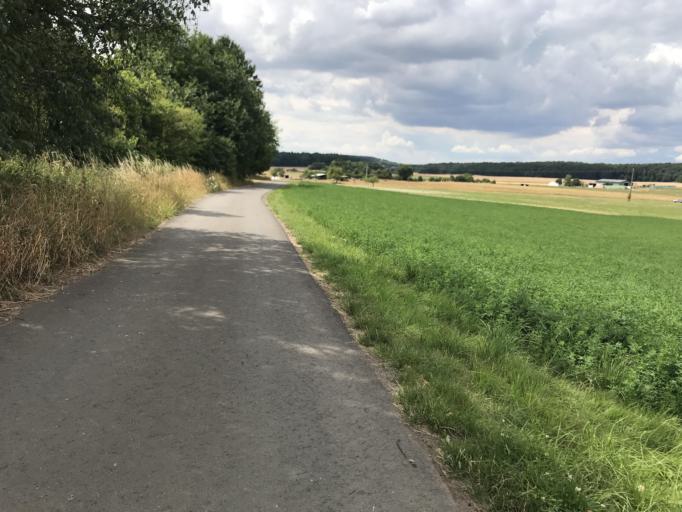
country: DE
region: Hesse
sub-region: Regierungsbezirk Giessen
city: Reiskirchen
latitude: 50.5745
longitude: 8.8827
